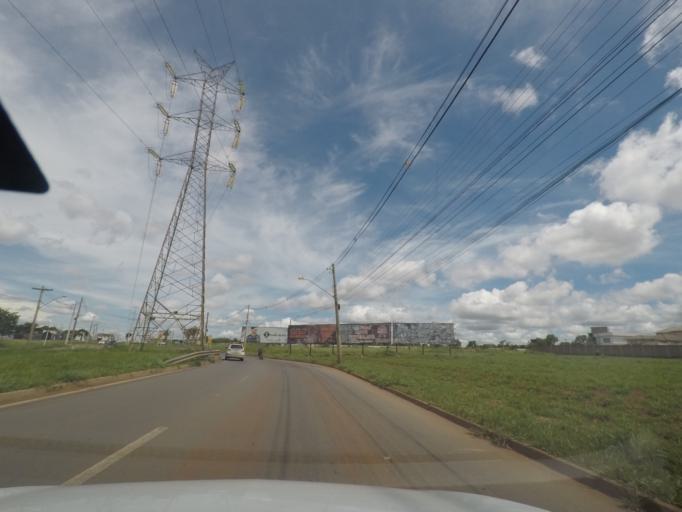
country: BR
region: Goias
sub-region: Goiania
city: Goiania
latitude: -16.7504
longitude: -49.3414
